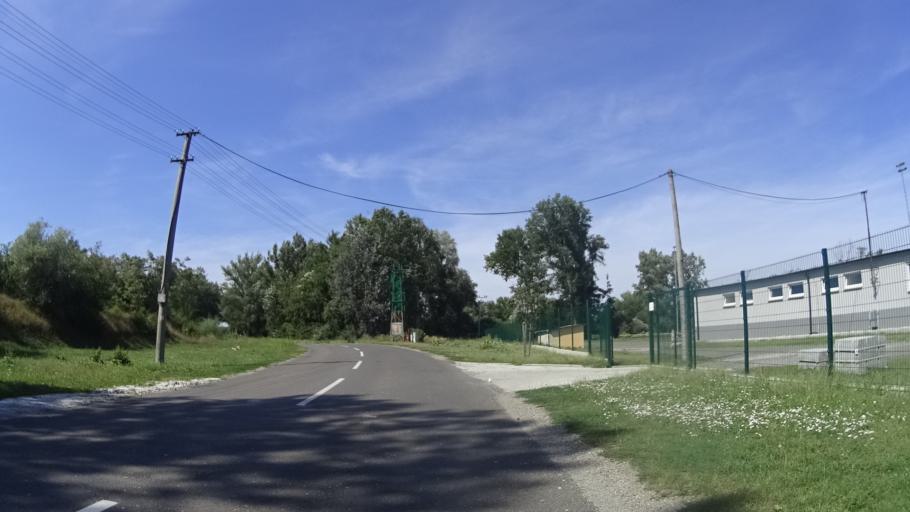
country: AT
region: Lower Austria
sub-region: Politischer Bezirk Ganserndorf
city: Marchegg
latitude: 48.3327
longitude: 16.9053
